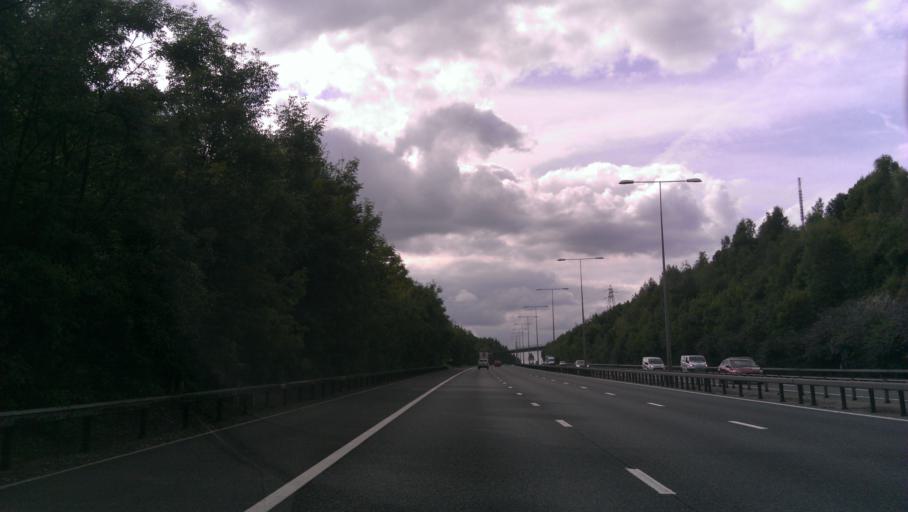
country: GB
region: England
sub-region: Kent
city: Borough Green
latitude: 51.3153
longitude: 0.2986
